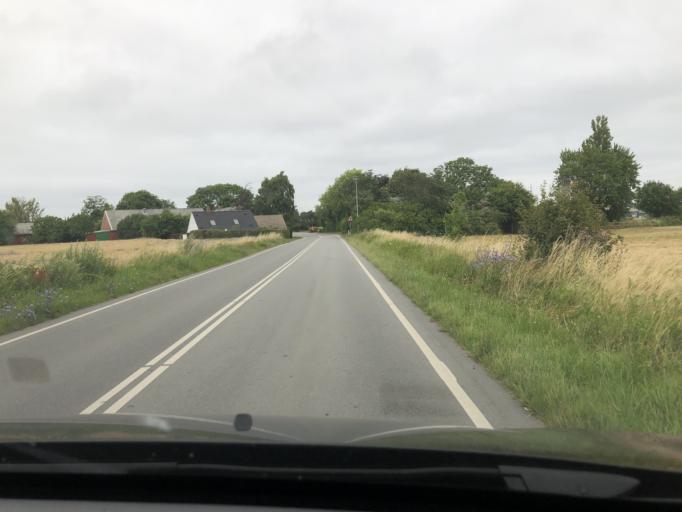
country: DK
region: South Denmark
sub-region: AEro Kommune
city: Marstal
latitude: 54.8479
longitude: 10.4968
